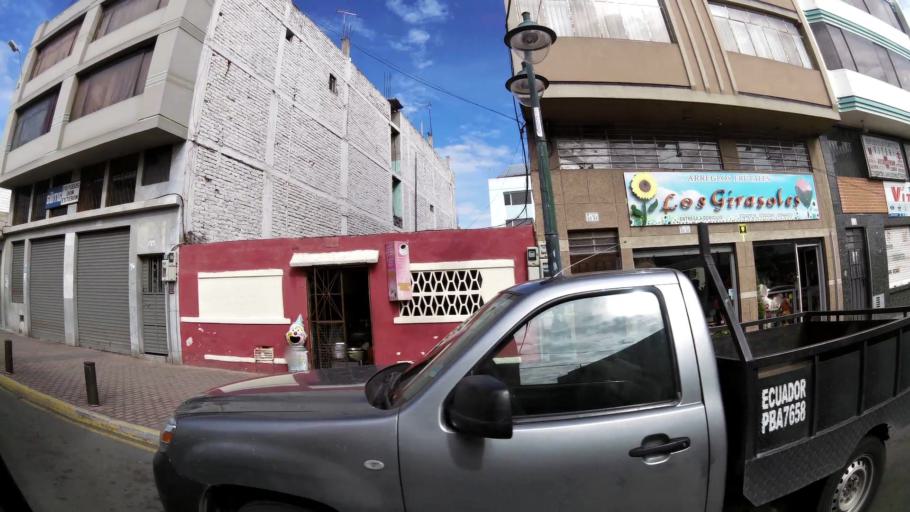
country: EC
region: Tungurahua
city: Ambato
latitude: -1.2279
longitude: -78.6319
